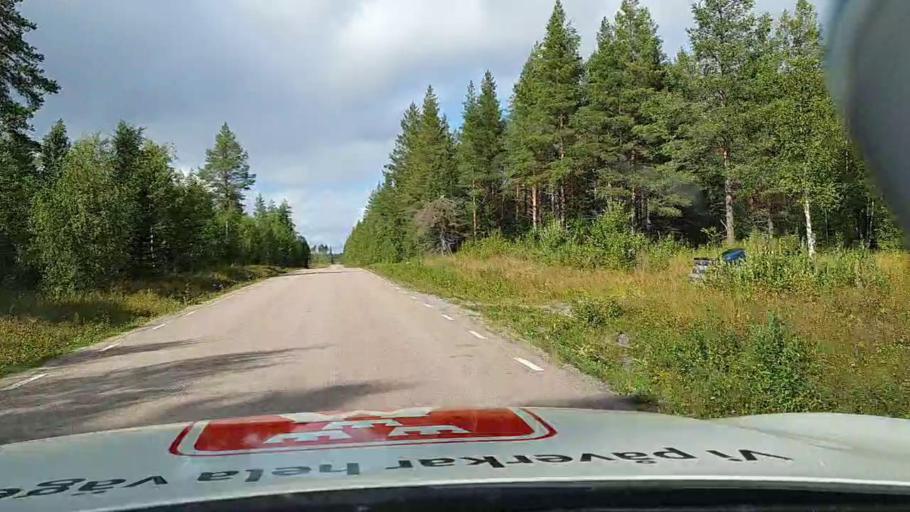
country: SE
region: Jaemtland
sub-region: Stroemsunds Kommun
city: Stroemsund
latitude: 63.8508
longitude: 15.3989
